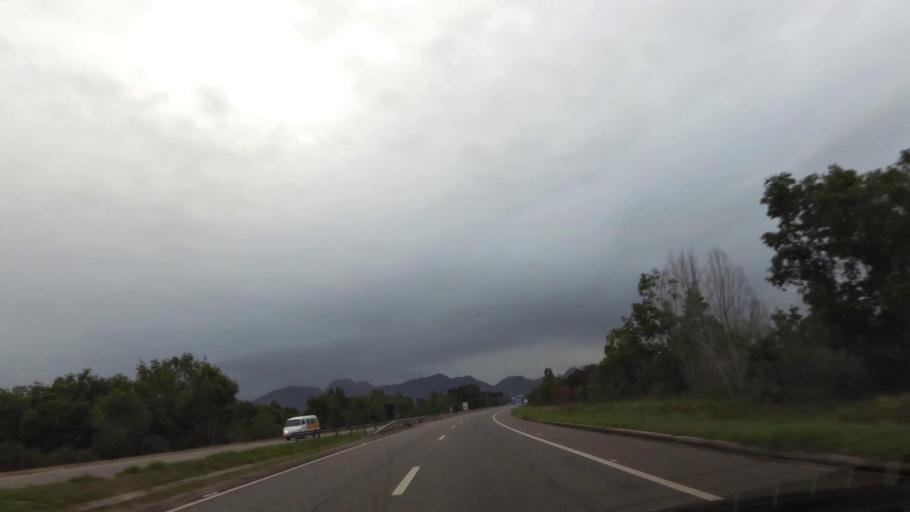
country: BR
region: Espirito Santo
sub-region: Guarapari
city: Guarapari
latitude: -20.6202
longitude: -40.4362
